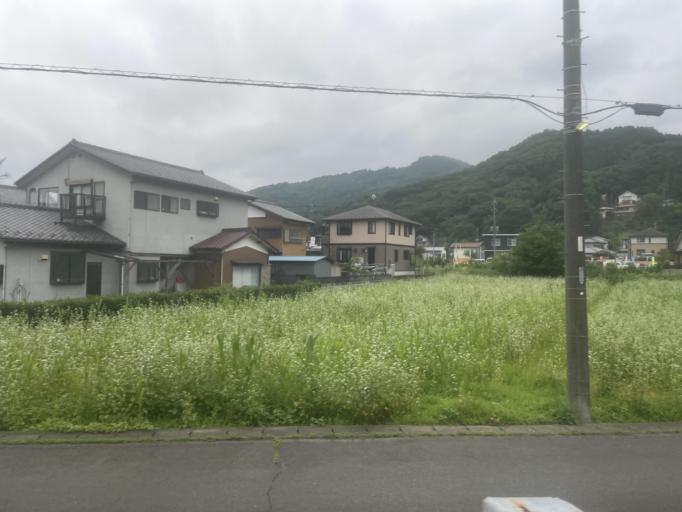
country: JP
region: Saitama
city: Yorii
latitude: 36.0966
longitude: 139.1114
